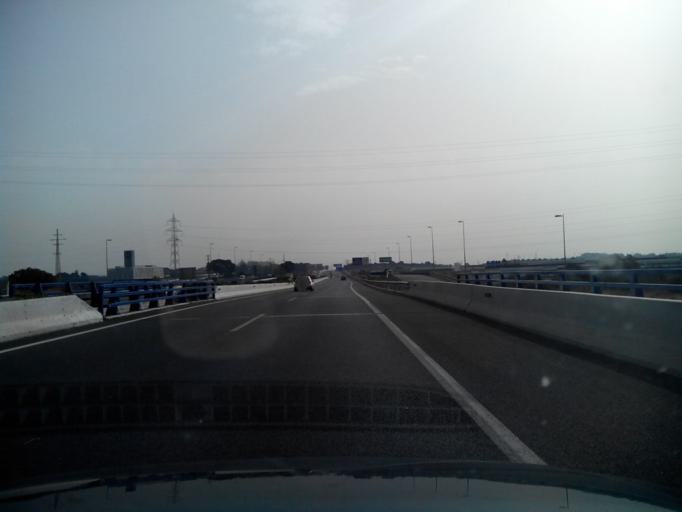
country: ES
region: Catalonia
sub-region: Provincia de Tarragona
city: Vila-seca
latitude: 41.1357
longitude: 1.1746
